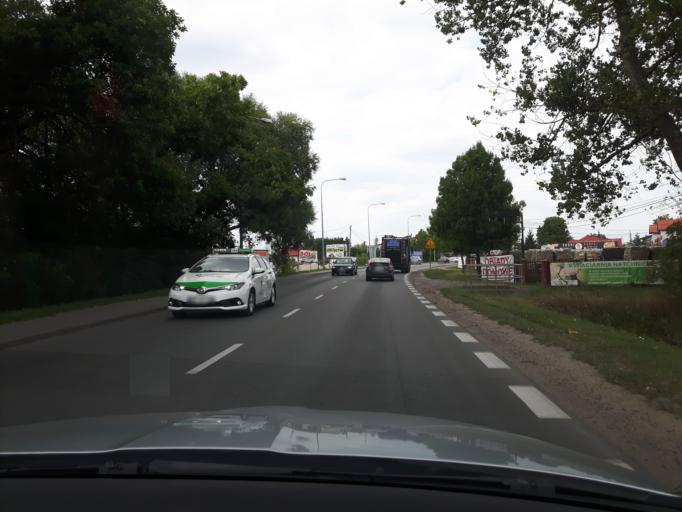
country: PL
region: Masovian Voivodeship
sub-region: Powiat legionowski
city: Stanislawow Pierwszy
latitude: 52.3536
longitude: 21.0287
